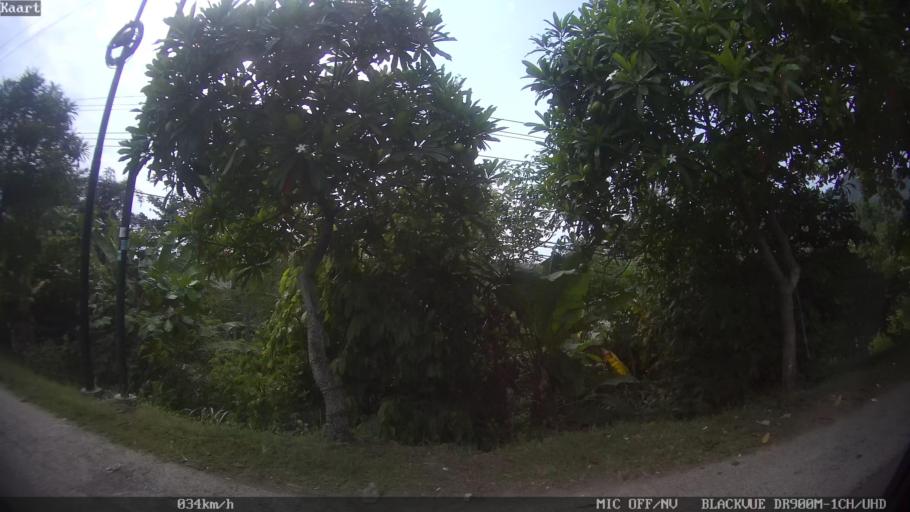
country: ID
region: Lampung
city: Bandarlampung
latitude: -5.4690
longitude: 105.2448
